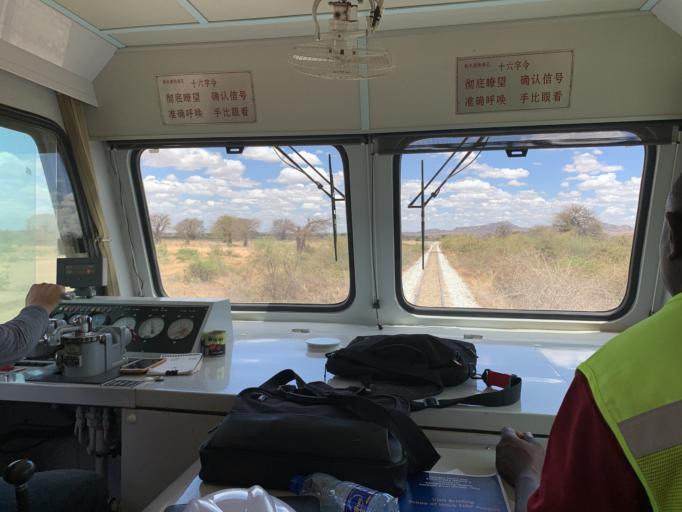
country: TZ
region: Dodoma
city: Dodoma
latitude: -6.1219
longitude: 35.5111
